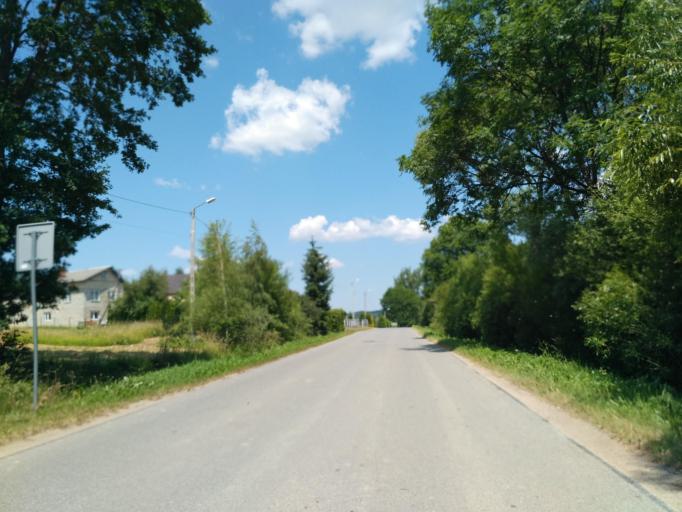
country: PL
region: Subcarpathian Voivodeship
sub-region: Powiat sanocki
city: Poraz
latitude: 49.4770
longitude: 22.1903
